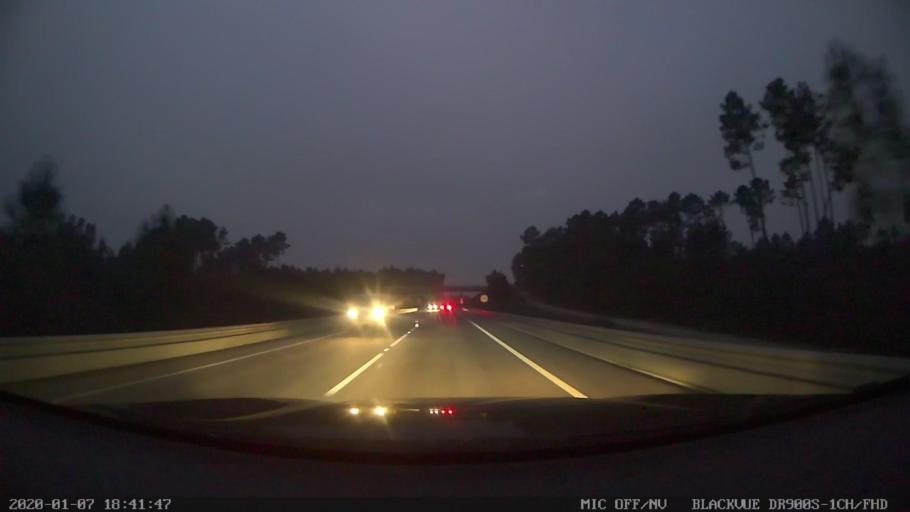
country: PT
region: Vila Real
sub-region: Vila Real
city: Vila Real
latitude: 41.2714
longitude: -7.6884
